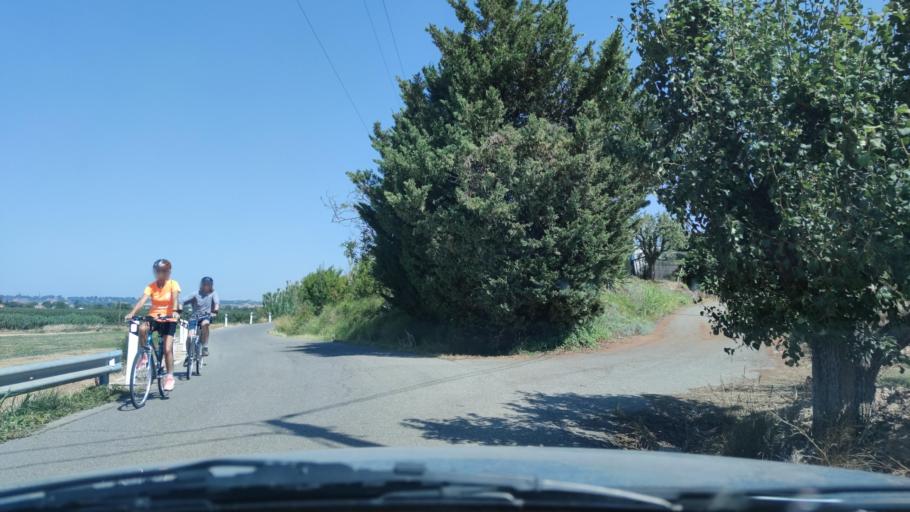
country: ES
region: Catalonia
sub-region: Provincia de Lleida
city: Torrefarrera
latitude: 41.6406
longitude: 0.5888
